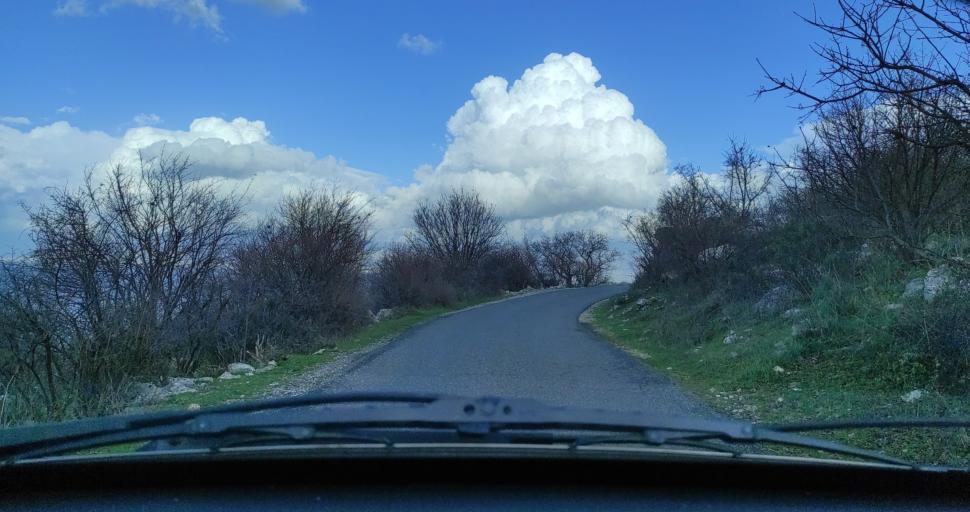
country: AL
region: Shkoder
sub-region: Rrethi i Shkodres
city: Dajc
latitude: 42.0690
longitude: 19.4172
